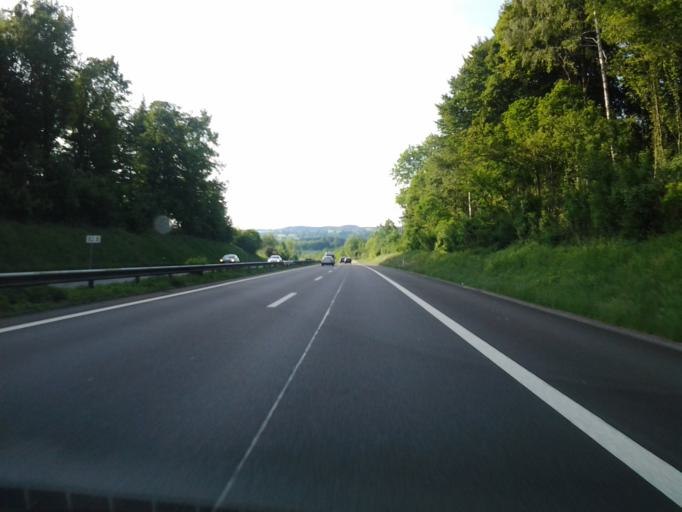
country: CH
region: Lucerne
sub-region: Sursee District
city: Hildisrieden
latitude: 47.1232
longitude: 8.2228
